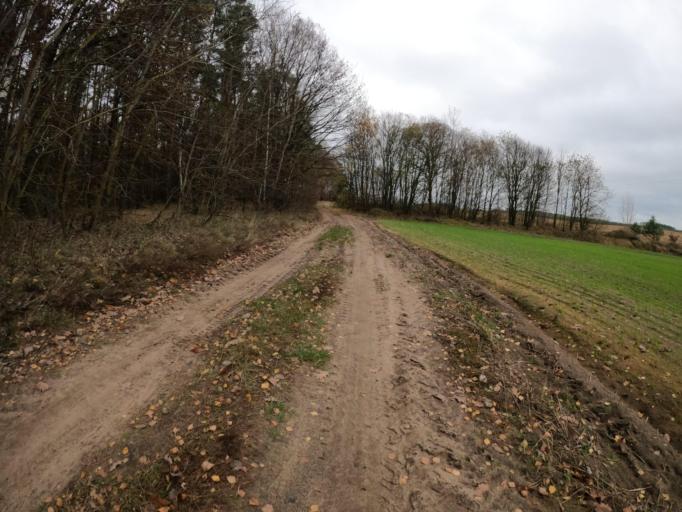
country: PL
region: West Pomeranian Voivodeship
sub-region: Powiat walecki
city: Miroslawiec
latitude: 53.2875
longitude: 16.1312
